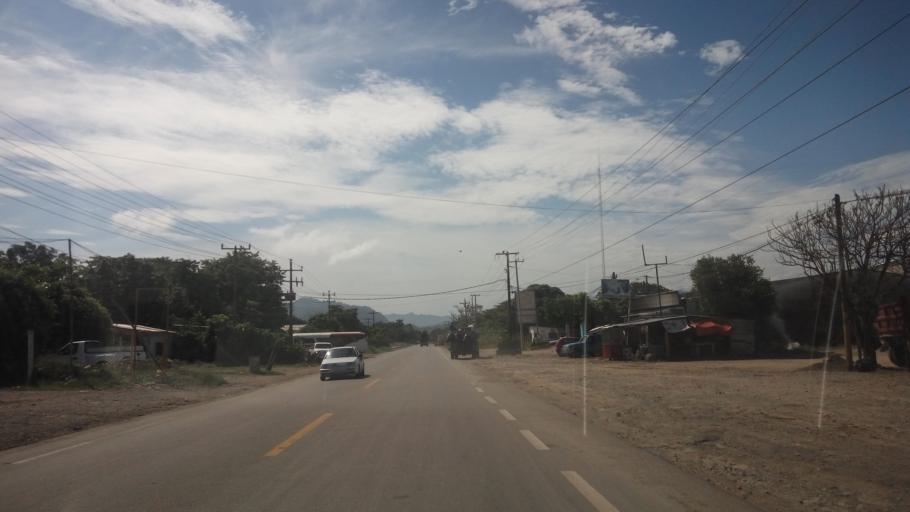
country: MX
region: Tabasco
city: Teapa
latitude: 17.5745
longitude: -92.9583
